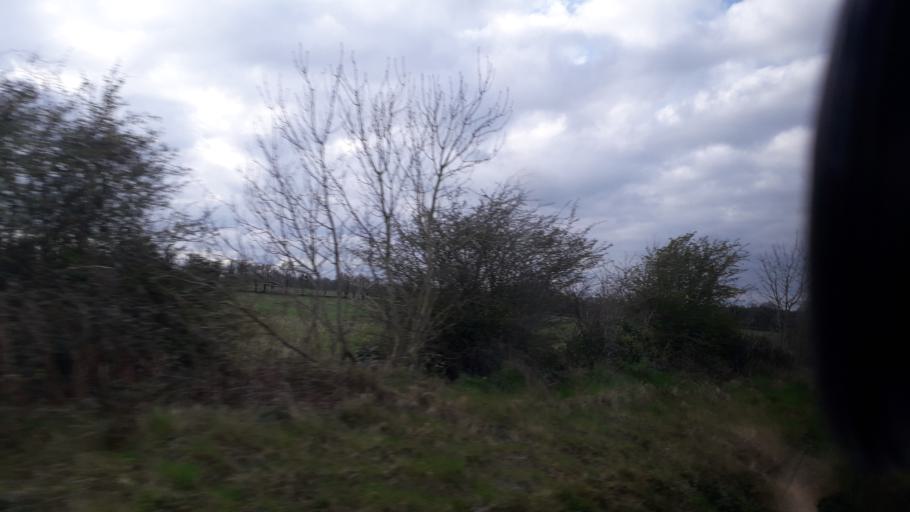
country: IE
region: Leinster
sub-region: An Iarmhi
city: An Muileann gCearr
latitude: 53.6132
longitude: -7.4084
